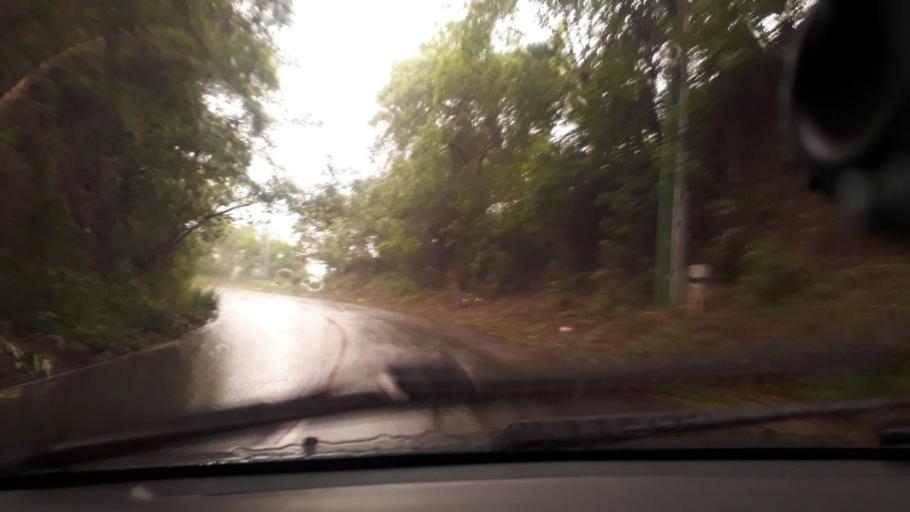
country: GT
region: Jutiapa
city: Comapa
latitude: 14.0277
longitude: -89.9074
